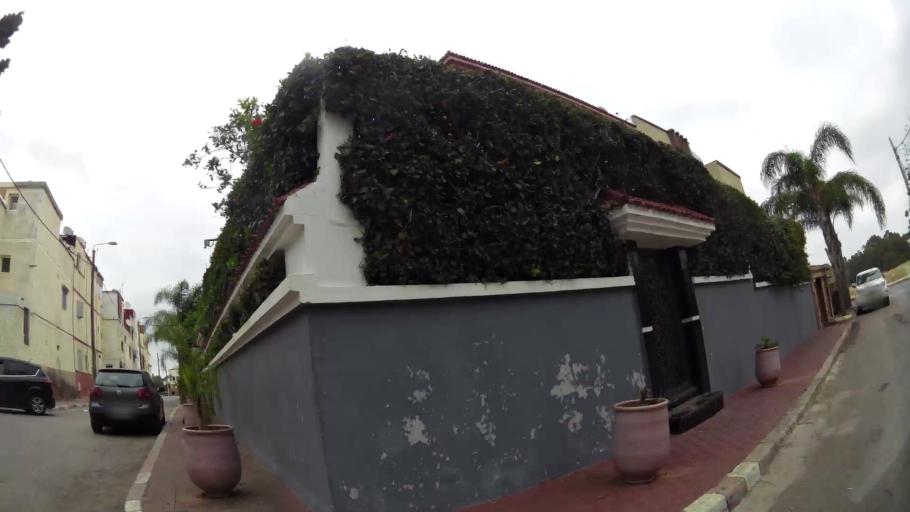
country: MA
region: Rabat-Sale-Zemmour-Zaer
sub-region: Rabat
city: Rabat
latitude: 33.9700
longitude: -6.8187
